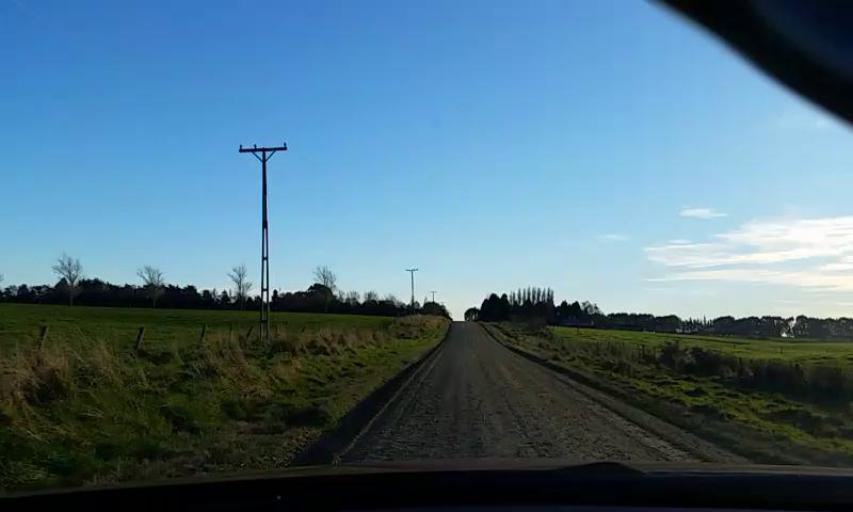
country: NZ
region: Southland
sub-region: Invercargill City
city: Invercargill
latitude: -46.2851
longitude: 168.5028
